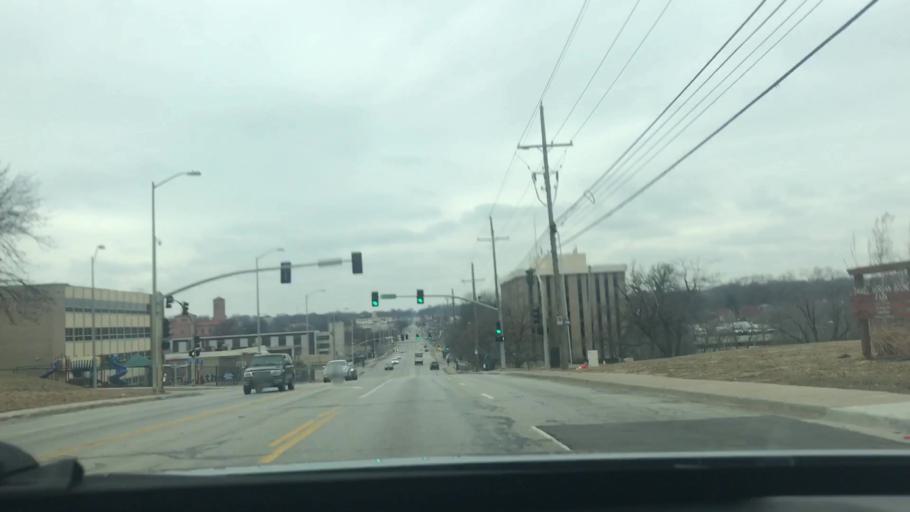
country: US
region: Kansas
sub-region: Johnson County
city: Mission Hills
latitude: 39.0128
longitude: -94.5624
